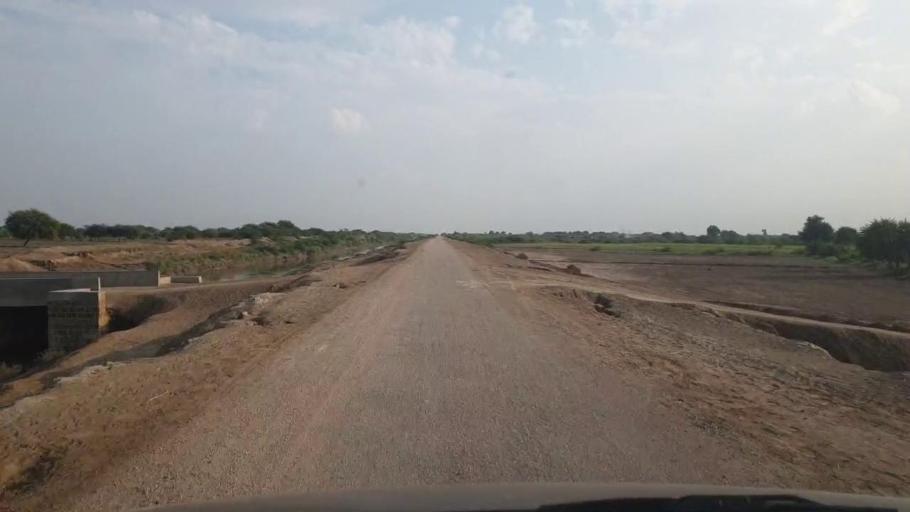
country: PK
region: Sindh
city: Badin
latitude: 24.5392
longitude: 68.6748
